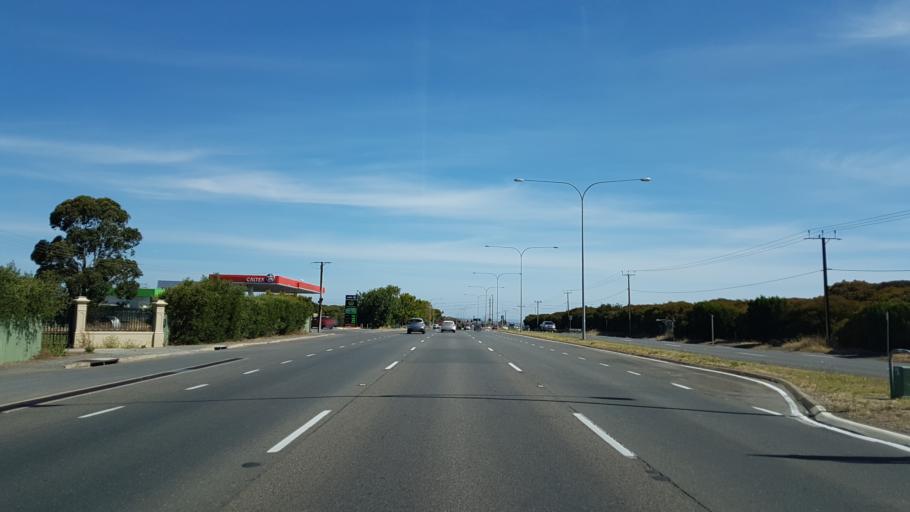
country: AU
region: South Australia
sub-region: Onkaparinga
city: Bedford Park
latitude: -35.0507
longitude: 138.5594
